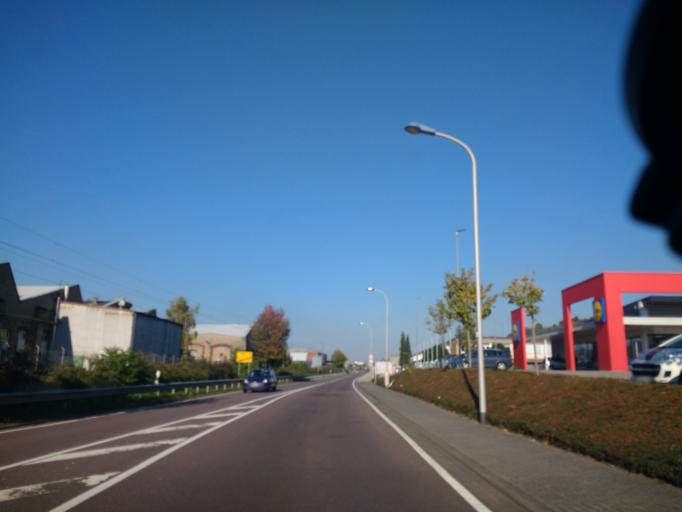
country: DE
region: Rheinland-Pfalz
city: Konz
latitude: 49.7004
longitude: 6.5805
